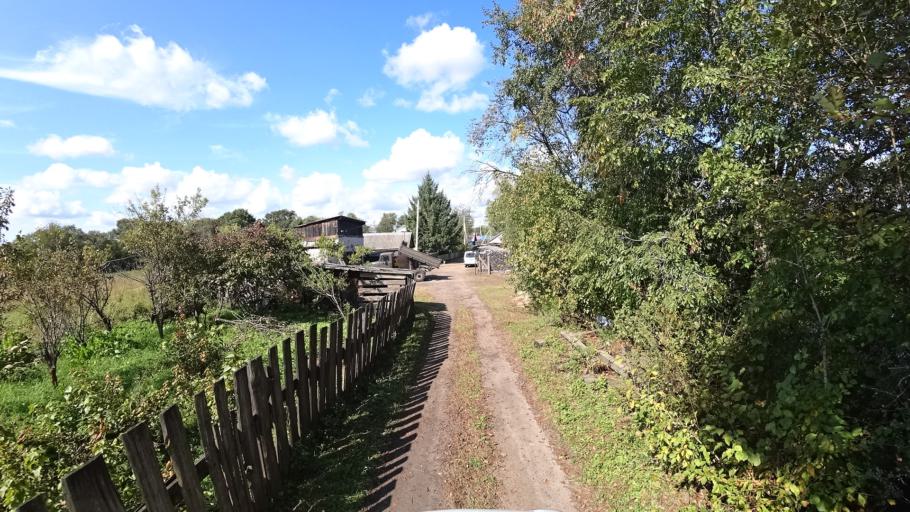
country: RU
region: Amur
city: Arkhara
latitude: 49.4019
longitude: 130.1557
